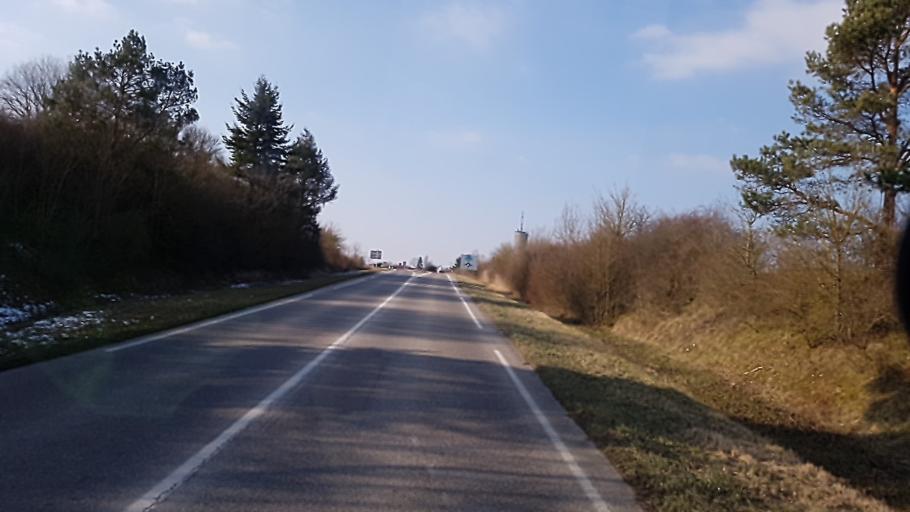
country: FR
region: Alsace
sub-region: Departement du Bas-Rhin
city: Drulingen
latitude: 48.8801
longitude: 7.1538
